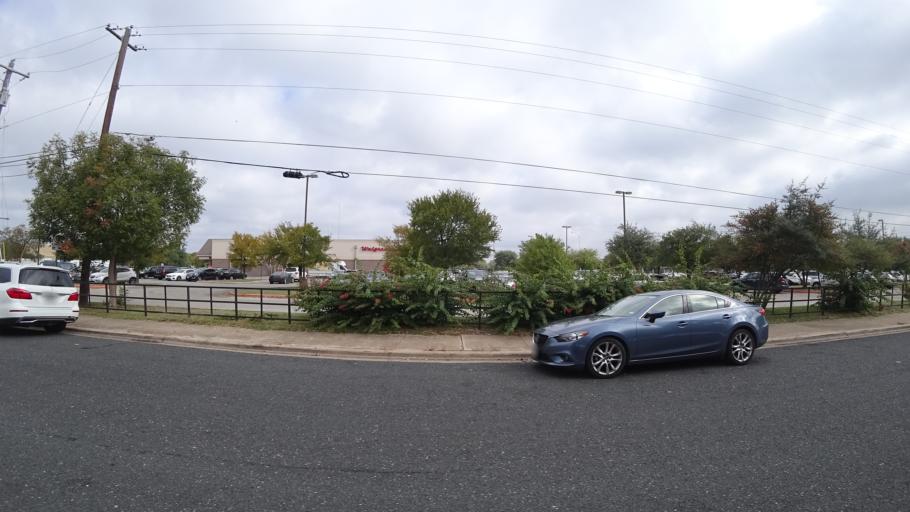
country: US
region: Texas
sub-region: Travis County
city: Shady Hollow
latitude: 30.2133
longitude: -97.8321
